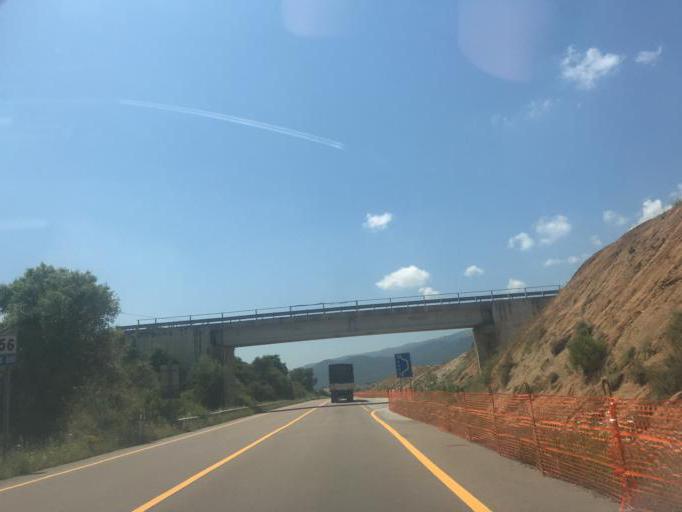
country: IT
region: Sardinia
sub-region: Provincia di Olbia-Tempio
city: Berchidda
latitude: 40.7800
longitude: 9.2279
